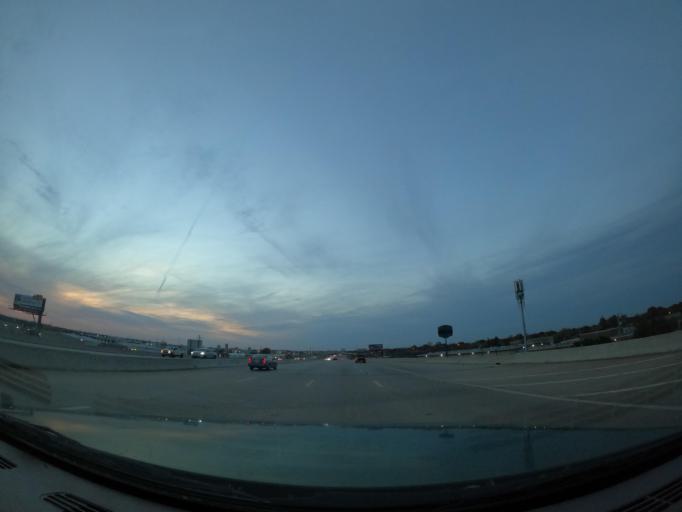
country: US
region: Oklahoma
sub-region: Tulsa County
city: Broken Arrow
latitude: 36.1017
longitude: -95.8690
